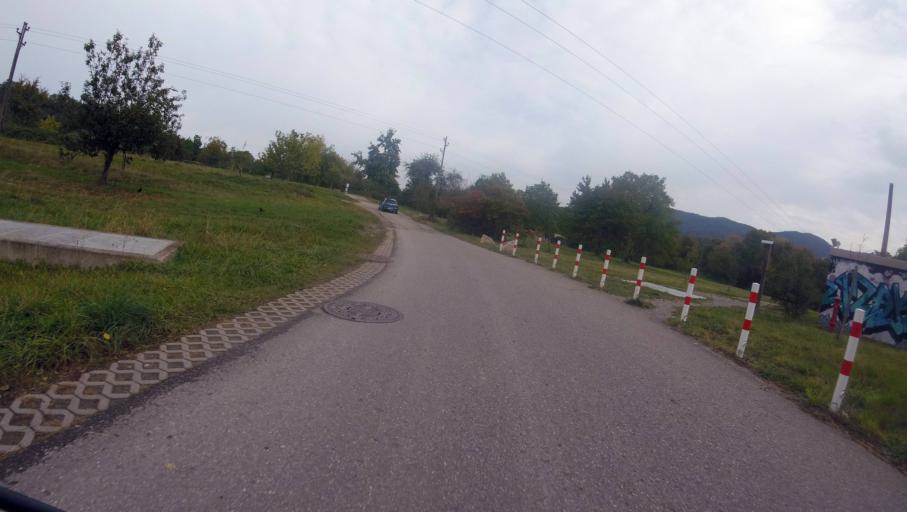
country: DE
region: Baden-Wuerttemberg
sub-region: Karlsruhe Region
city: Gernsbach
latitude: 48.7734
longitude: 8.3364
